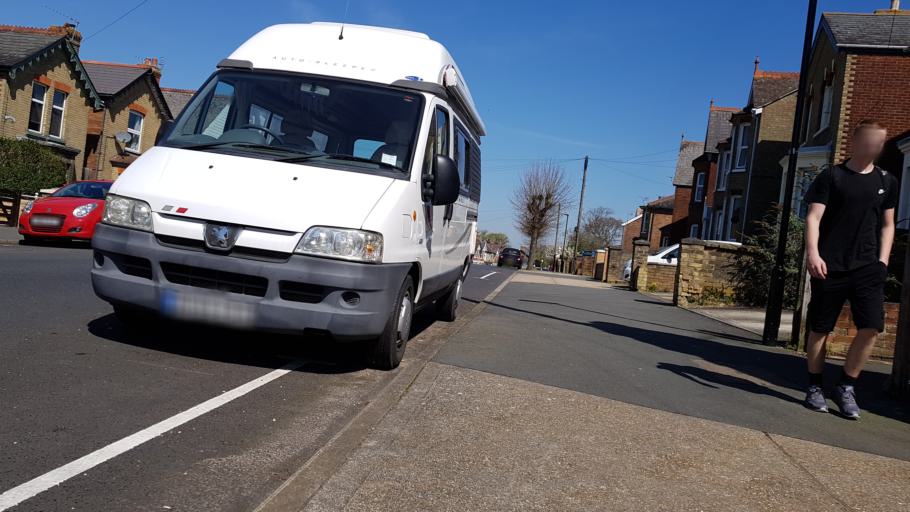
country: GB
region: England
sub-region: Isle of Wight
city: East Cowes
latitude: 50.7544
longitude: -1.2864
